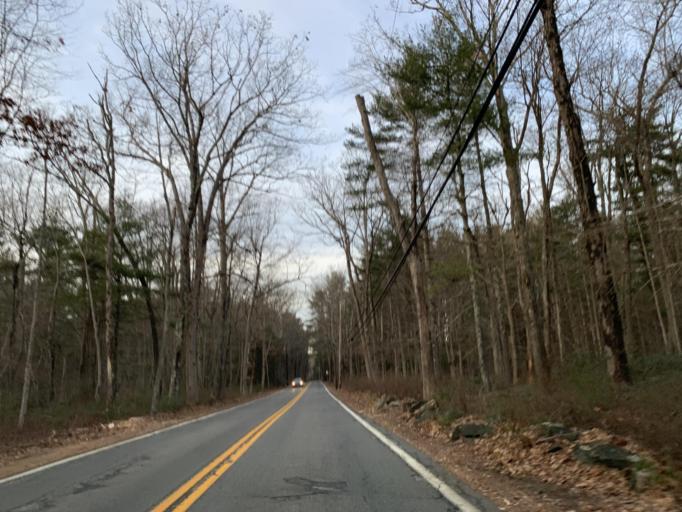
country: US
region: Rhode Island
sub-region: Providence County
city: Pascoag
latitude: 41.9281
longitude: -71.6995
